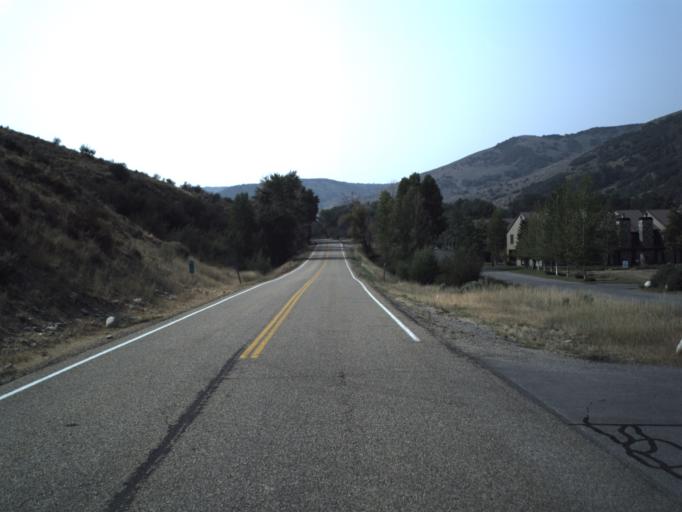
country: US
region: Utah
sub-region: Summit County
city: Summit Park
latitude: 40.8725
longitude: -111.5828
